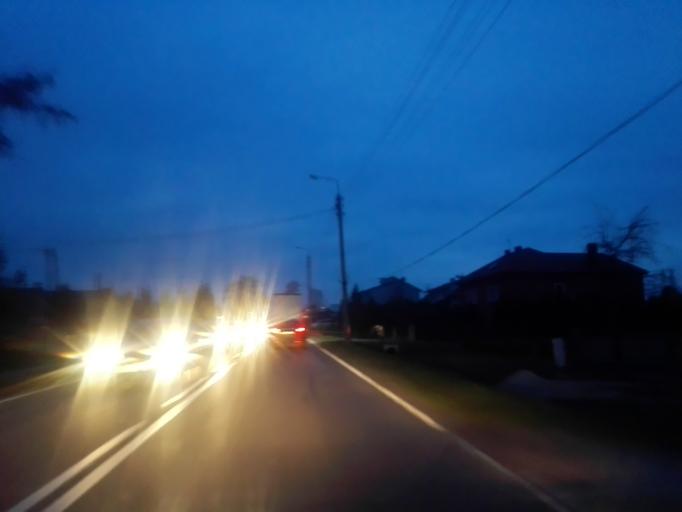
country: PL
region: Podlasie
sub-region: Lomza
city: Lomza
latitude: 53.1252
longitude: 22.0357
